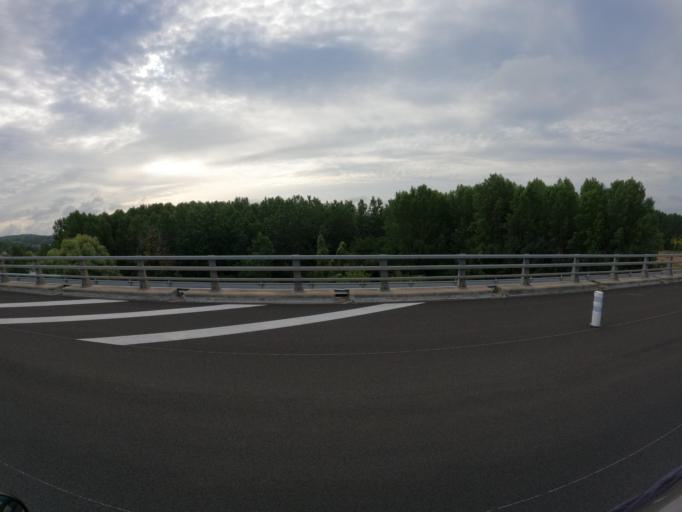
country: FR
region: Centre
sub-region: Departement d'Indre-et-Loire
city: Restigne
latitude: 47.2814
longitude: 0.2790
